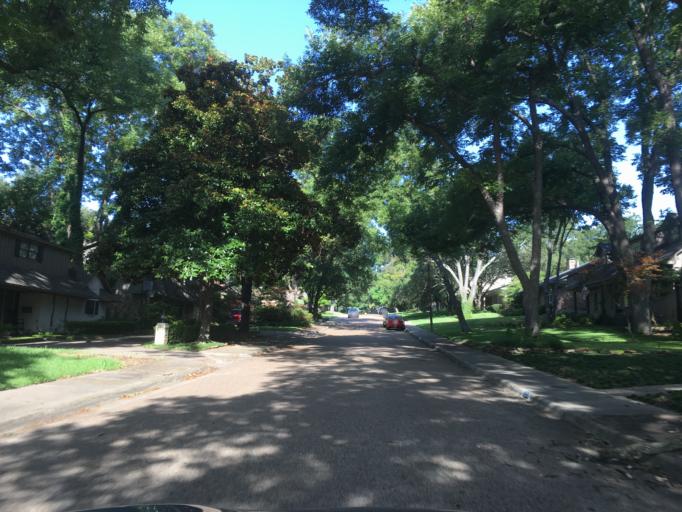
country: US
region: Texas
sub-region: Dallas County
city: Richardson
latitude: 32.8830
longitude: -96.7203
